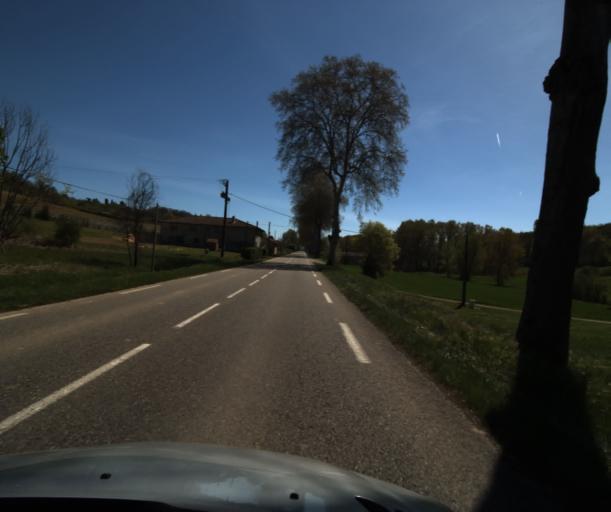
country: FR
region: Midi-Pyrenees
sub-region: Departement du Tarn-et-Garonne
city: Lafrancaise
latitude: 44.1322
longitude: 1.2223
